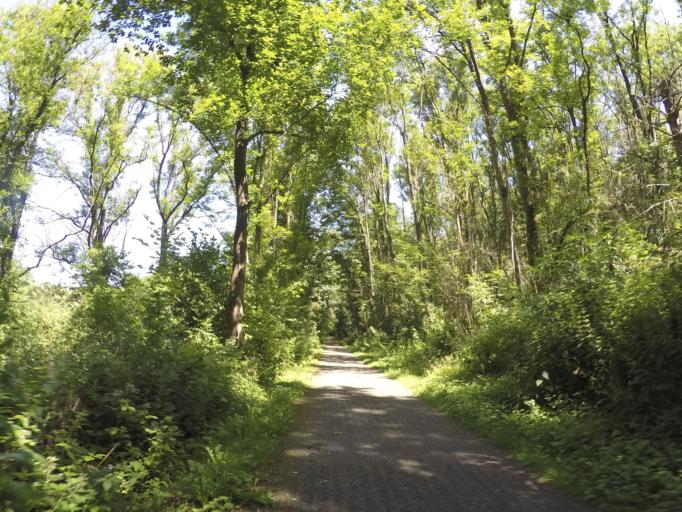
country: BE
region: Wallonia
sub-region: Province de Namur
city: Hamois
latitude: 50.3271
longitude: 5.1290
